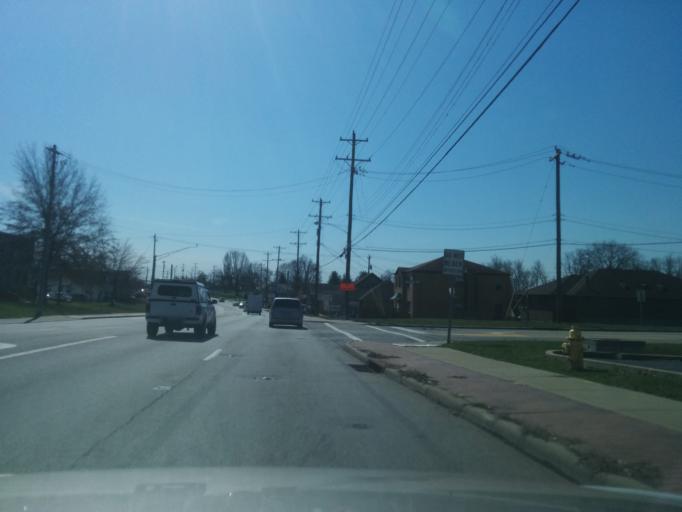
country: US
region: Ohio
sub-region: Hamilton County
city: Monfort Heights
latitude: 39.1828
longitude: -84.6043
